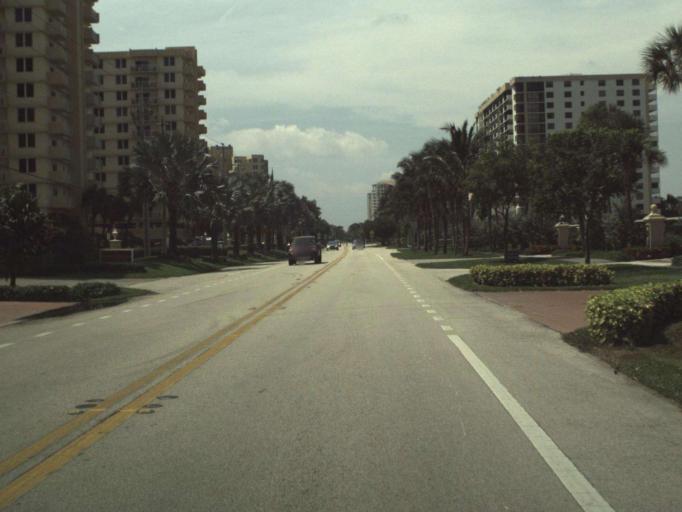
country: US
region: Florida
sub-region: Palm Beach County
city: Highland Beach
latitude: 26.4176
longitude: -80.0647
